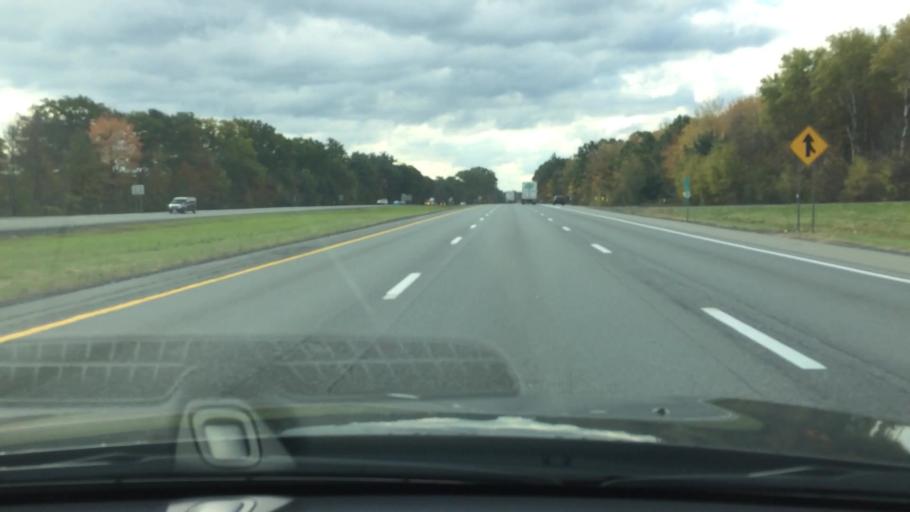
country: US
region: New York
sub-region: Saratoga County
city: Country Knolls
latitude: 42.9692
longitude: -73.8020
